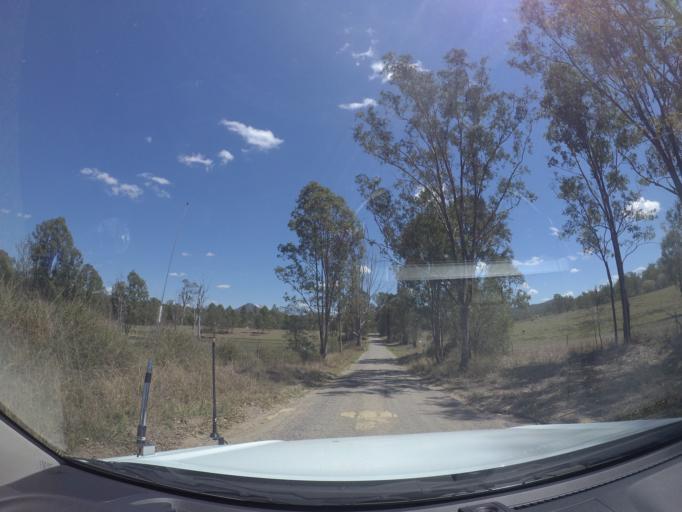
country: AU
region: Queensland
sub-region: Logan
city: Cedar Vale
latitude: -27.8467
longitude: 152.8821
